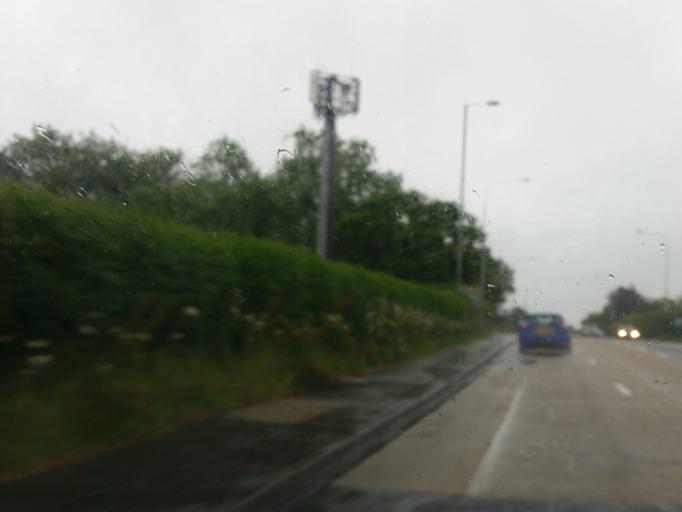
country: GB
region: Northern Ireland
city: Holywood
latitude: 54.6568
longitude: -5.7656
